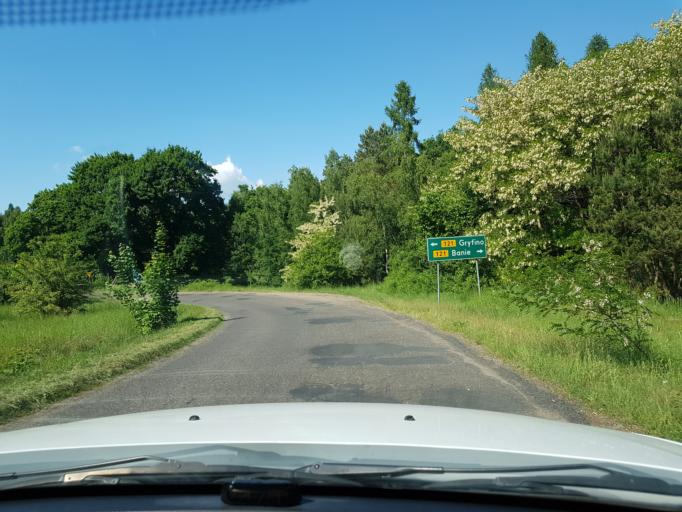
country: PL
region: West Pomeranian Voivodeship
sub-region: Powiat gryfinski
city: Gryfino
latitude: 53.1804
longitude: 14.5494
